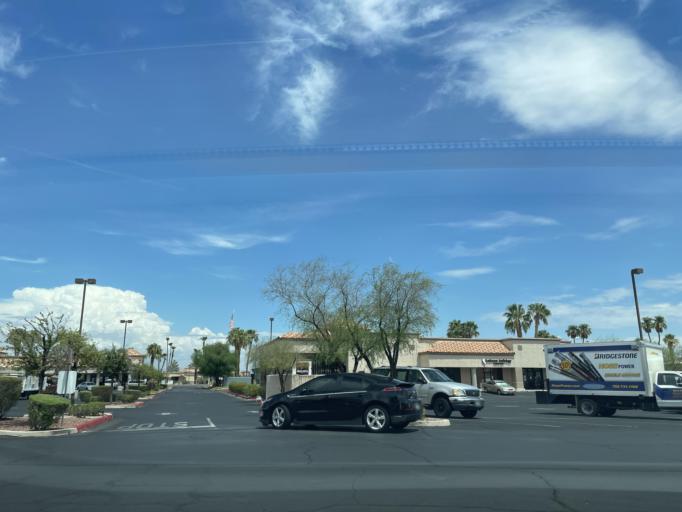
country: US
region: Nevada
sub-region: Clark County
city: Whitney
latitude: 36.0409
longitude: -115.1012
